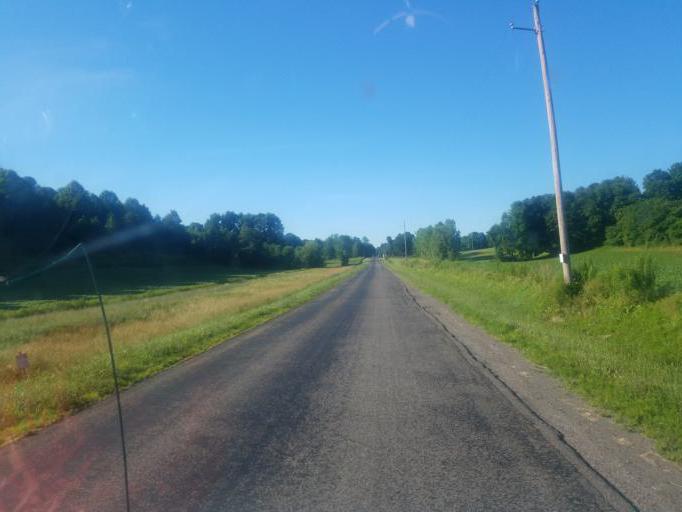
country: US
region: New York
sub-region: Wayne County
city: Lyons
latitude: 43.1093
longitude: -77.0459
